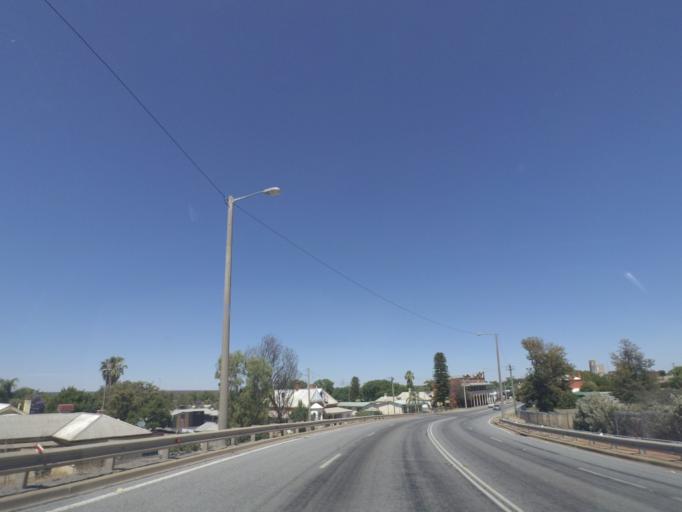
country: AU
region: New South Wales
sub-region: Narrandera
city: Narrandera
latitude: -34.7410
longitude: 146.5587
